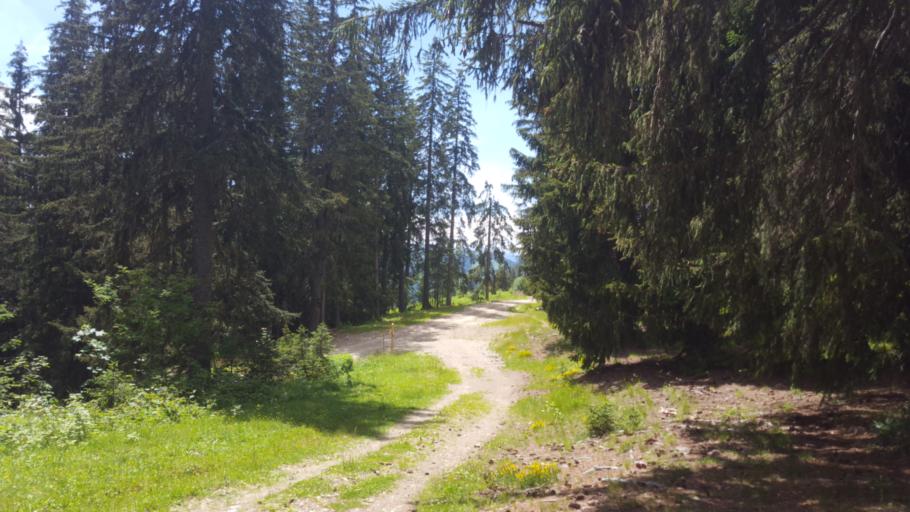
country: FR
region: Rhone-Alpes
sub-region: Departement de la Haute-Savoie
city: Le Grand-Bornand
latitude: 45.9195
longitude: 6.4561
